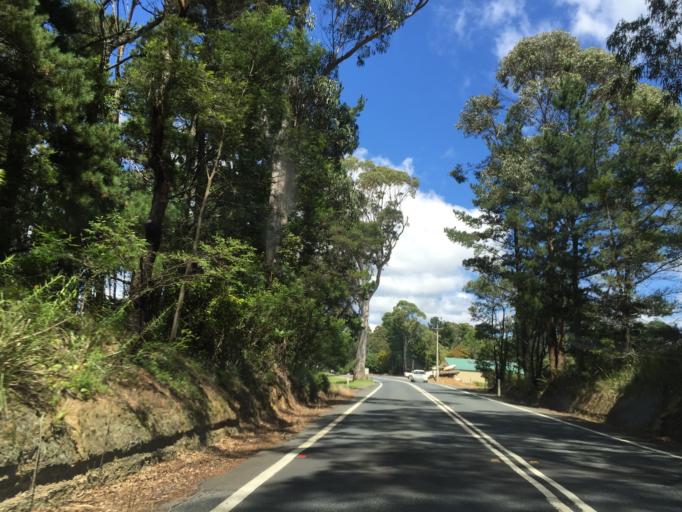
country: AU
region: New South Wales
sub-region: Blue Mountains Municipality
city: Lawson
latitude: -33.5208
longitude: 150.4626
